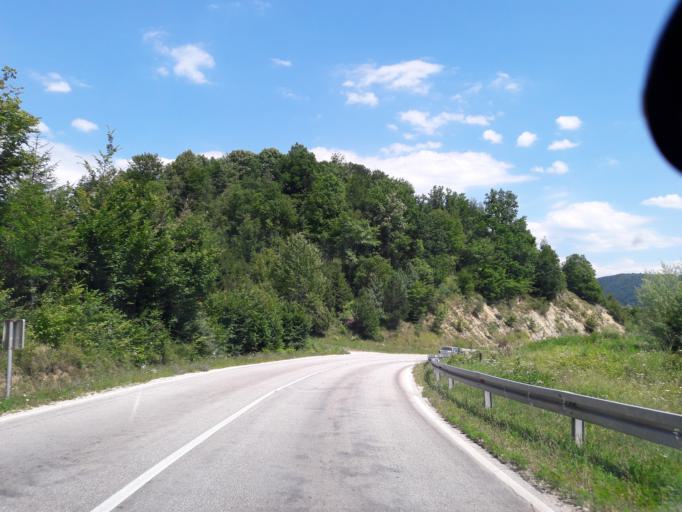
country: BA
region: Republika Srpska
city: Mrkonjic Grad
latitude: 44.4183
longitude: 17.1002
